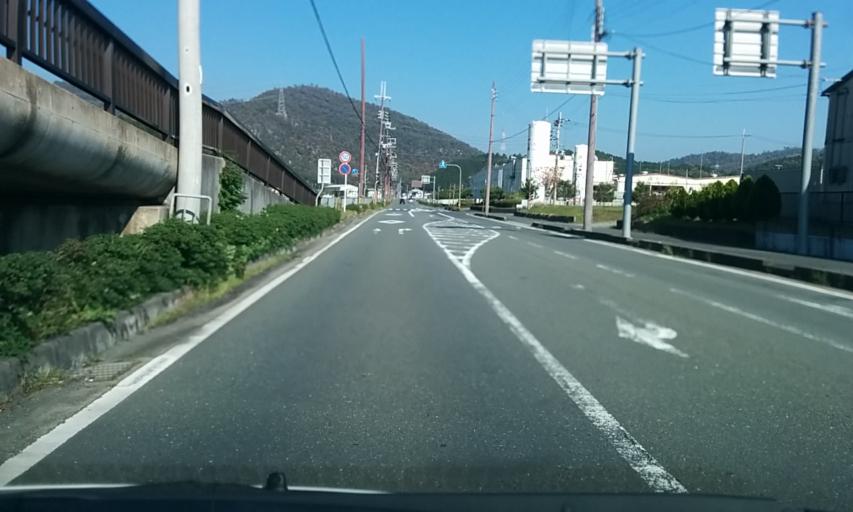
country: JP
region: Kyoto
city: Kameoka
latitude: 35.1252
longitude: 135.4826
